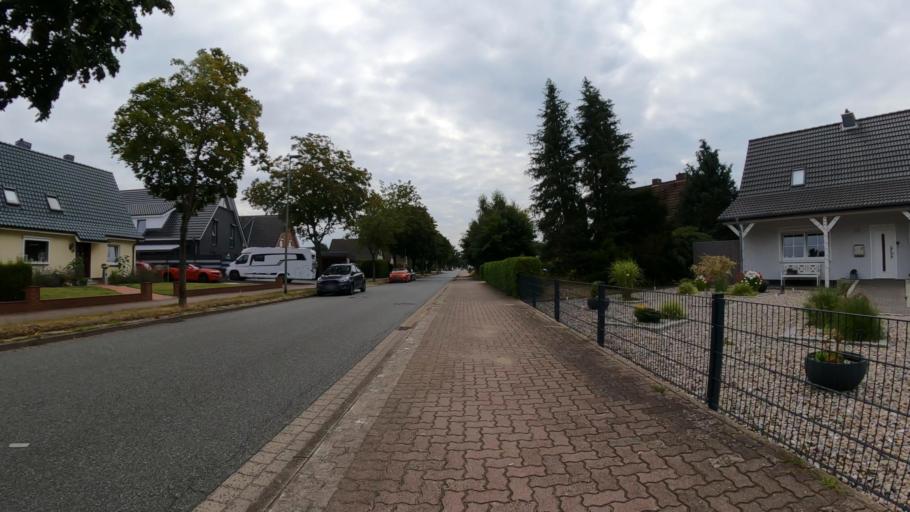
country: DE
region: Schleswig-Holstein
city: Boostedt
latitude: 54.0518
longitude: 10.0331
